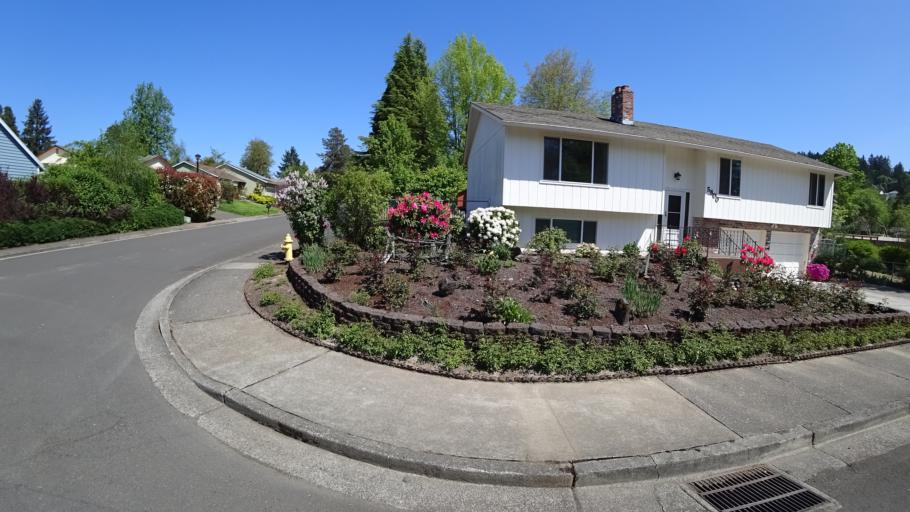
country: US
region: Oregon
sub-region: Washington County
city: Aloha
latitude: 45.4780
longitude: -122.8492
